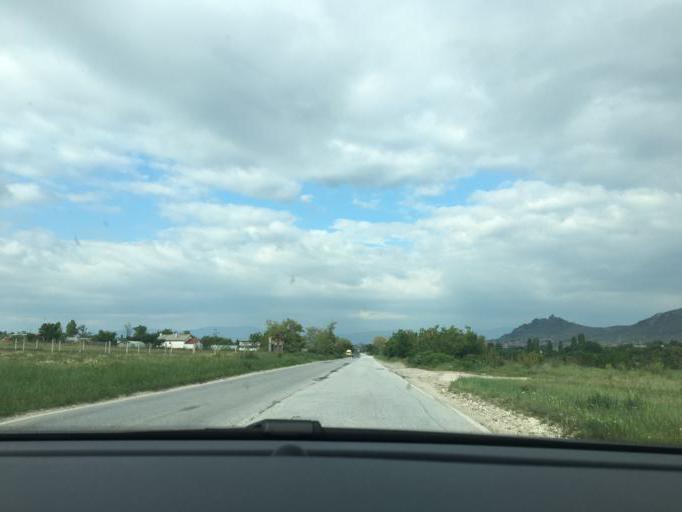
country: MK
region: Prilep
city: Prilep
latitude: 41.3627
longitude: 21.6018
